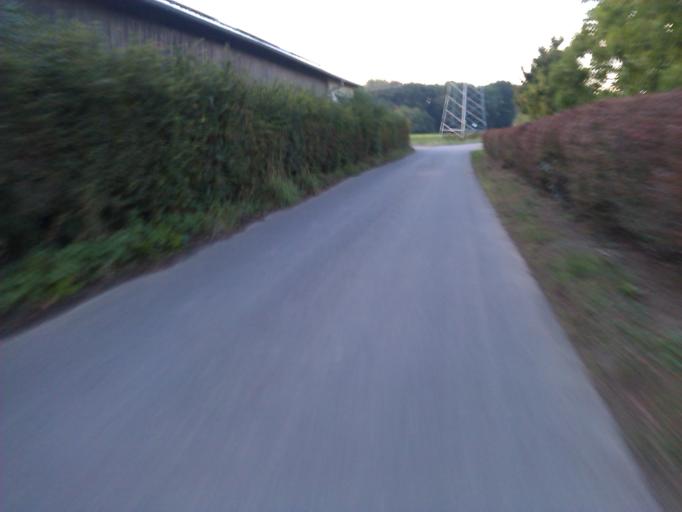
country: DE
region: Baden-Wuerttemberg
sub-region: Regierungsbezirk Stuttgart
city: Talheim
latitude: 49.1037
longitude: 9.1668
